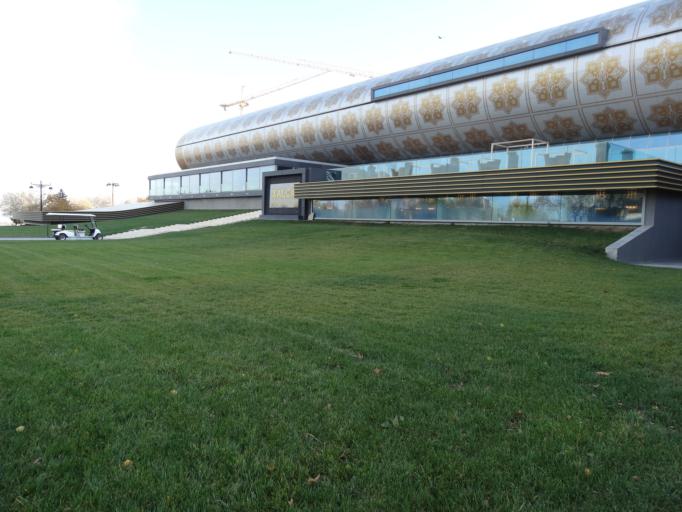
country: AZ
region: Baki
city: Badamdar
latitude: 40.3602
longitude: 49.8354
